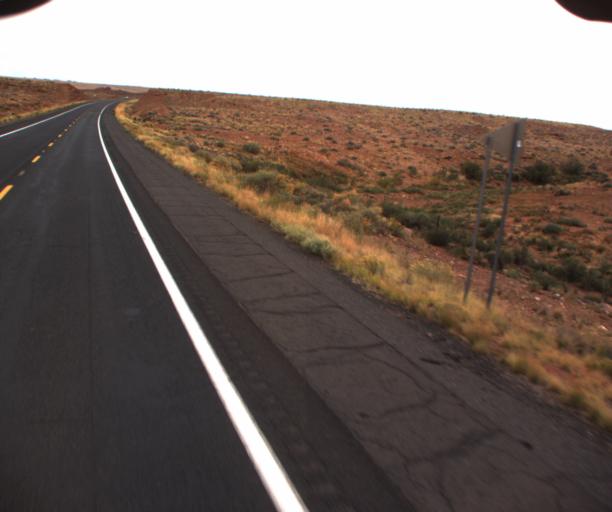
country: US
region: Arizona
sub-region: Coconino County
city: Tuba City
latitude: 35.7892
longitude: -111.4506
